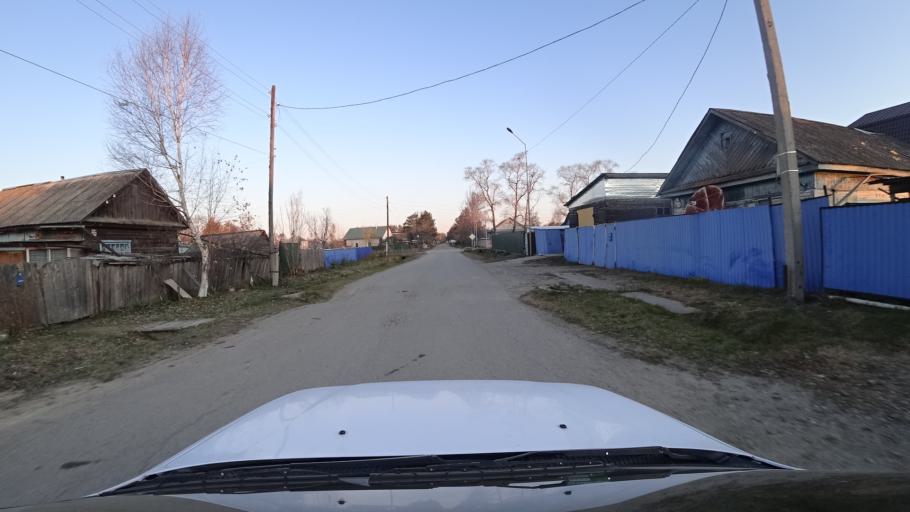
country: RU
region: Primorskiy
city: Dal'nerechensk
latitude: 45.9232
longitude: 133.7368
